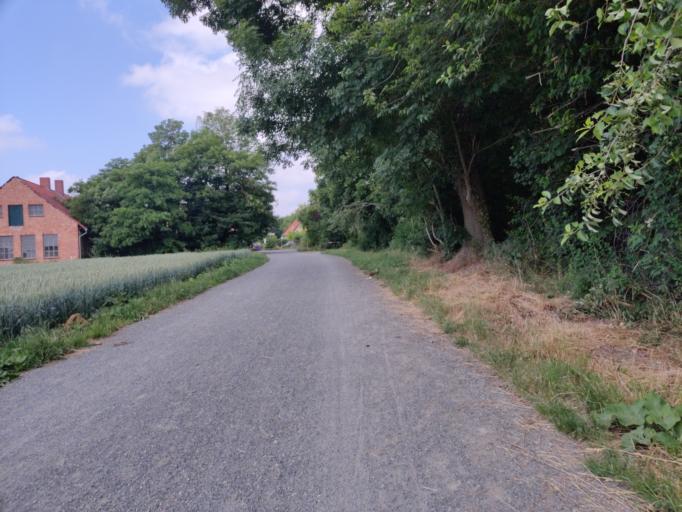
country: DE
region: Lower Saxony
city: Hildesheim
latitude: 52.1139
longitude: 9.9815
